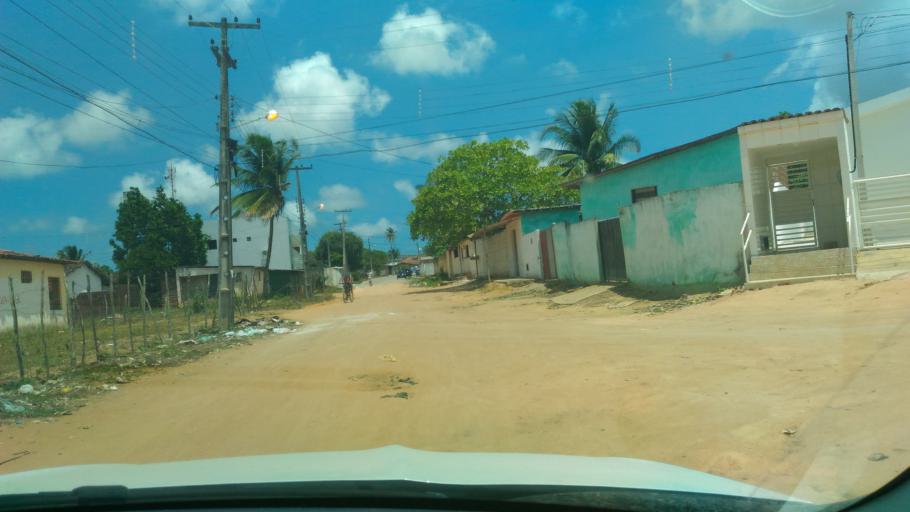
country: BR
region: Paraiba
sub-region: Conde
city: Conde
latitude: -7.2632
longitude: -34.9109
